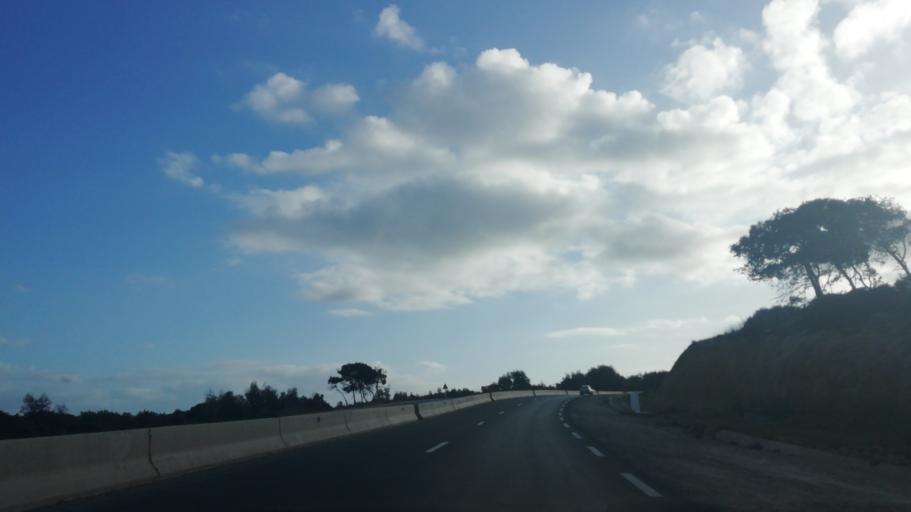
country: DZ
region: Mostaganem
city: Mostaganem
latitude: 36.1138
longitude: 0.2399
